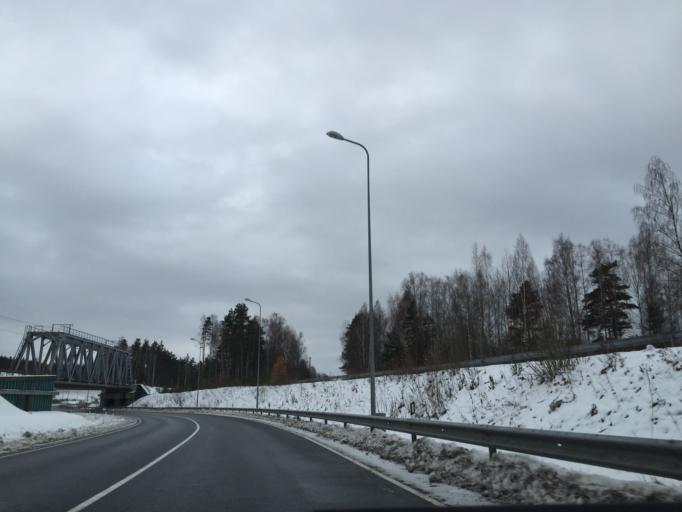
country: LV
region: Saulkrastu
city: Saulkrasti
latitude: 57.1978
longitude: 24.3649
